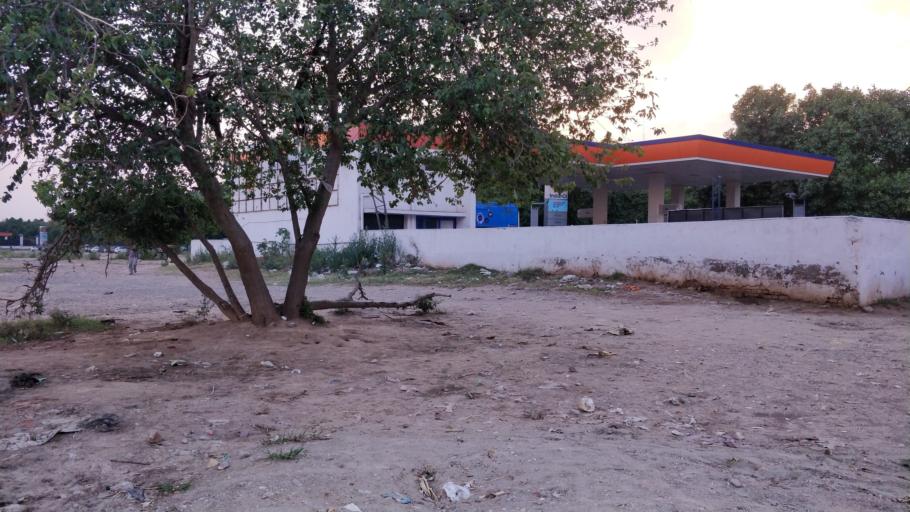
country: IN
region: Chandigarh
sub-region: Chandigarh
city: Chandigarh
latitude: 30.7200
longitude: 76.7709
